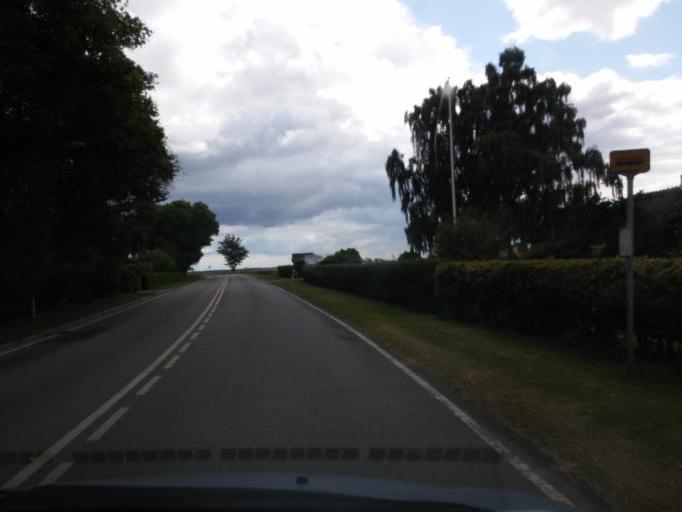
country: DK
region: South Denmark
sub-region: Kerteminde Kommune
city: Kerteminde
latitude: 55.4304
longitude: 10.6246
